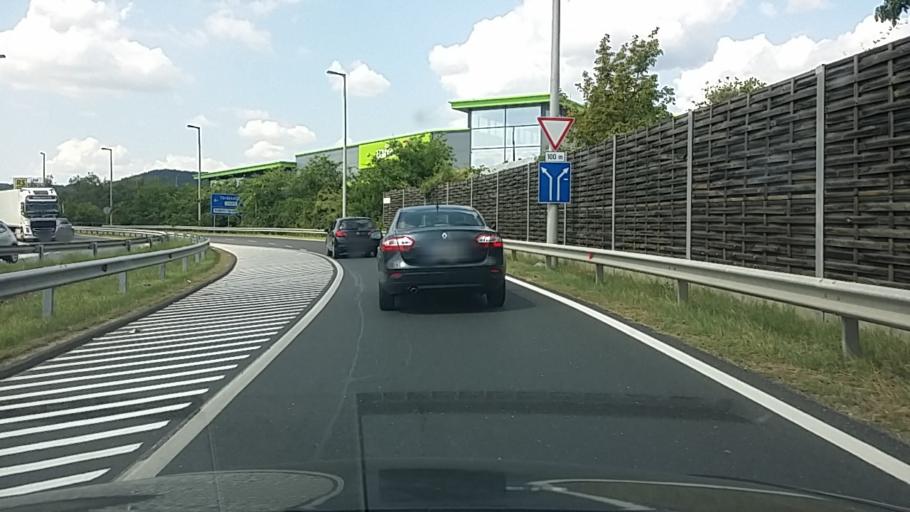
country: HU
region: Pest
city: Budaors
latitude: 47.4534
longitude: 18.9507
